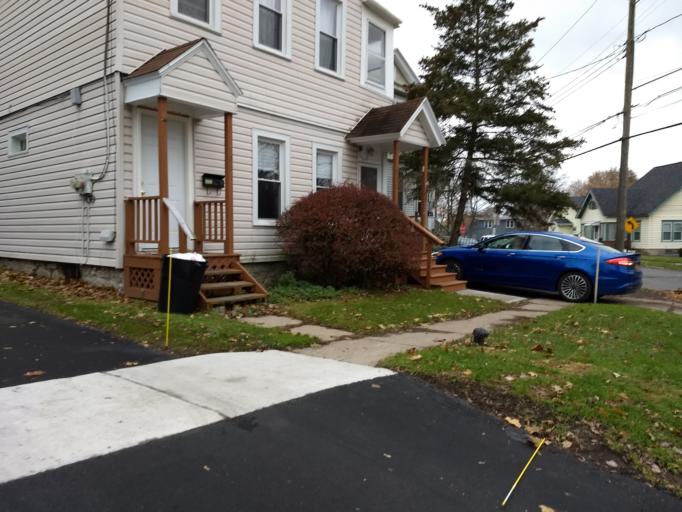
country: US
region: New York
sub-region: Onondaga County
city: Lyncourt
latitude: 43.0774
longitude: -76.1421
